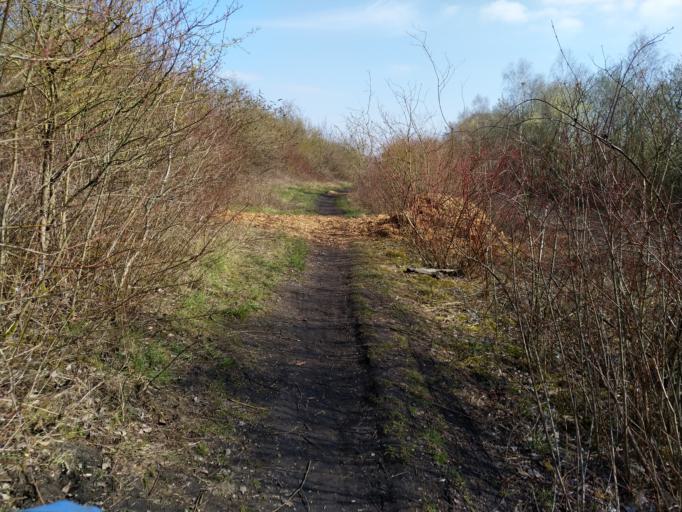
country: BE
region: Wallonia
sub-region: Province du Hainaut
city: Chasse Royale
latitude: 50.4277
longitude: 3.9452
